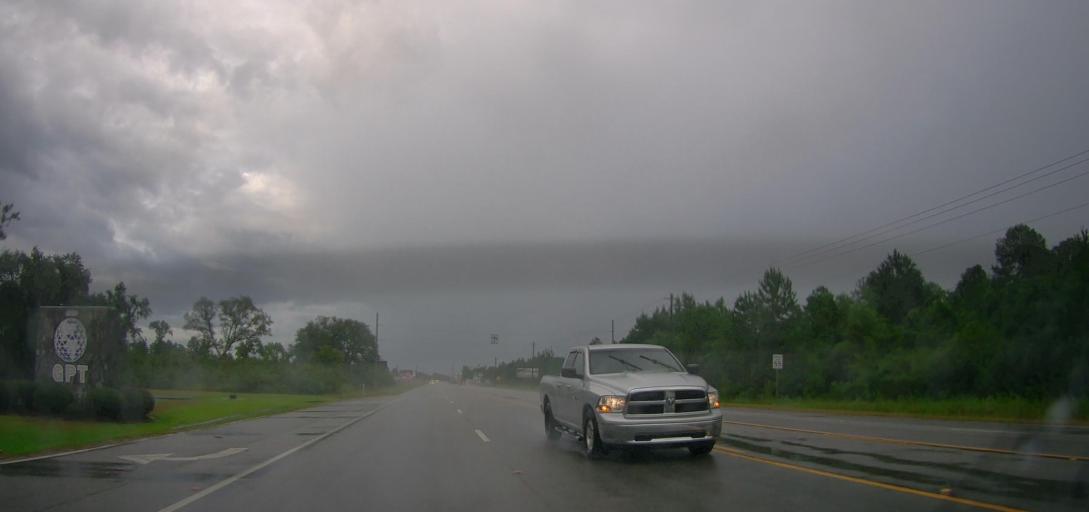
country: US
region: Georgia
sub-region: Ware County
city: Sunnyside
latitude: 31.2444
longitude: -82.3158
